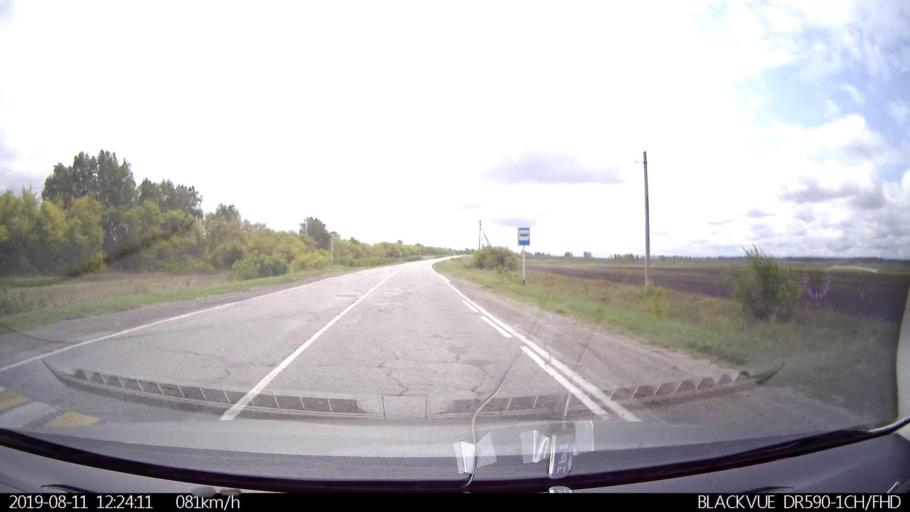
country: RU
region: Ulyanovsk
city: Ignatovka
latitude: 53.8864
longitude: 47.9499
